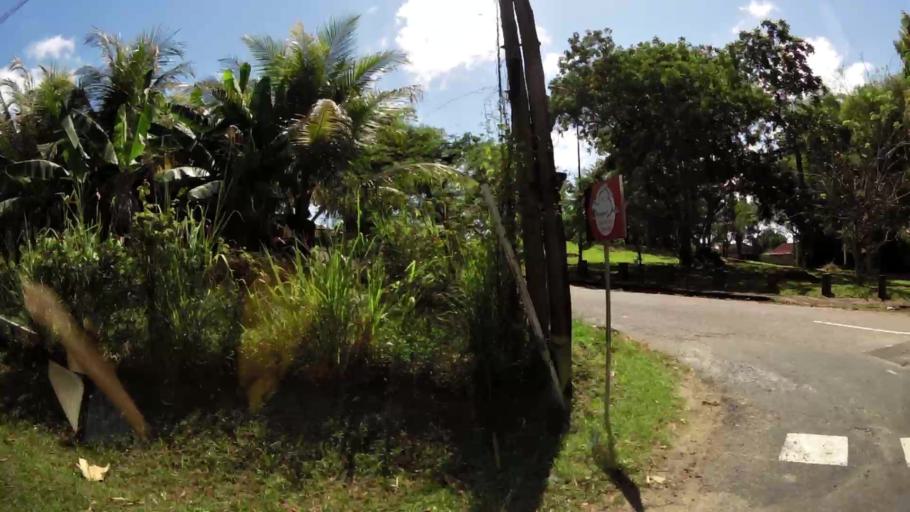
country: GF
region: Guyane
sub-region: Guyane
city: Matoury
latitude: 4.8485
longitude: -52.3316
